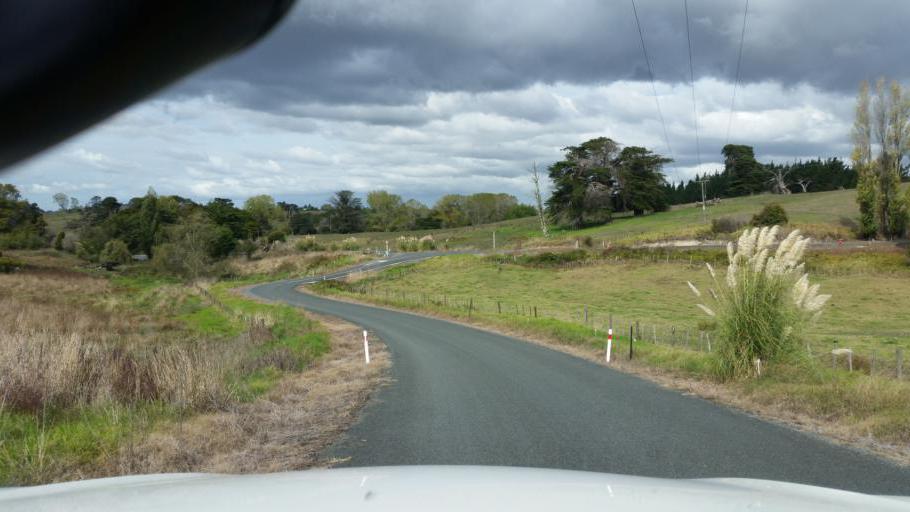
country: NZ
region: Northland
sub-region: Whangarei
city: Ruakaka
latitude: -36.1100
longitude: 174.2778
